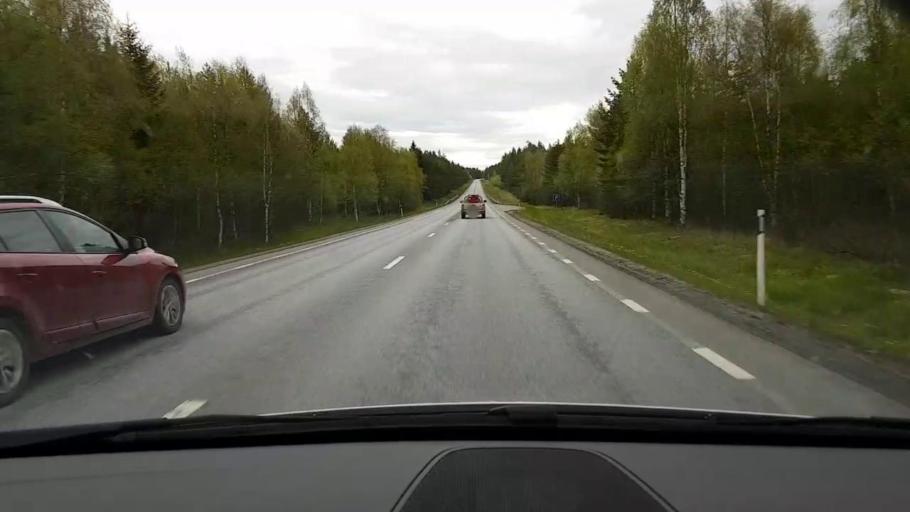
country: SE
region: Jaemtland
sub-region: Krokoms Kommun
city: Krokom
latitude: 63.3222
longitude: 14.2613
